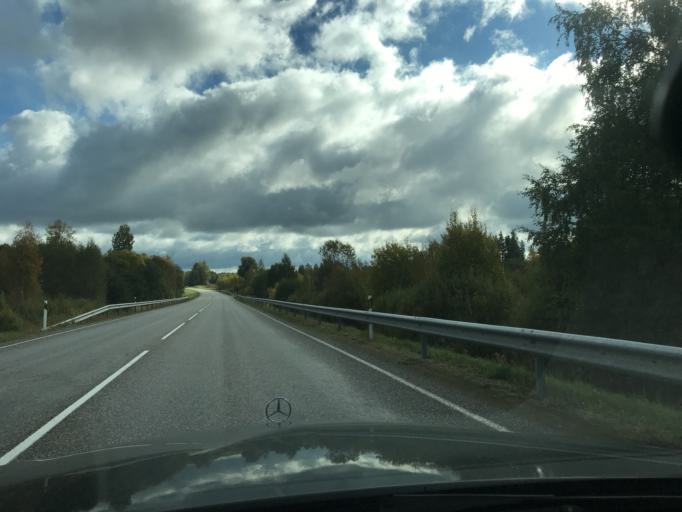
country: EE
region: Vorumaa
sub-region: Voru linn
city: Voru
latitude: 57.7547
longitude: 27.2219
